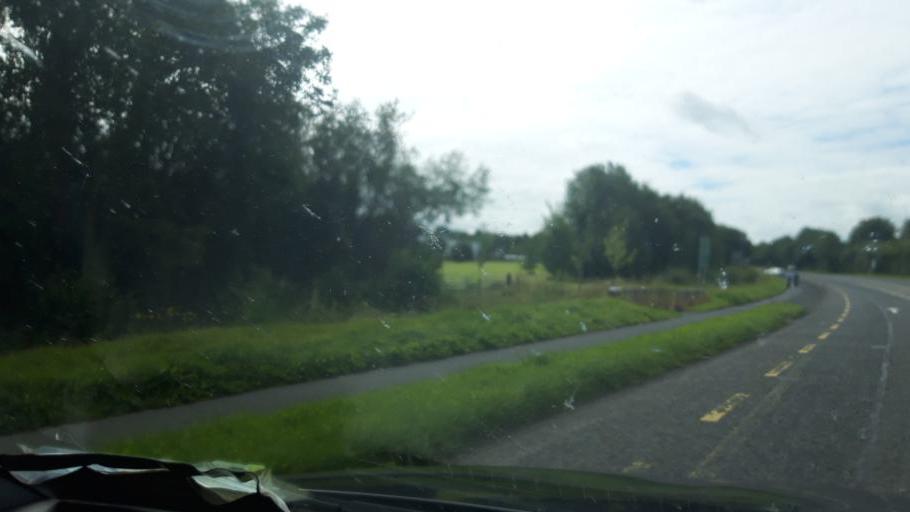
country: IE
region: Leinster
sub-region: Kilkenny
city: Callan
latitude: 52.5460
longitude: -7.3959
